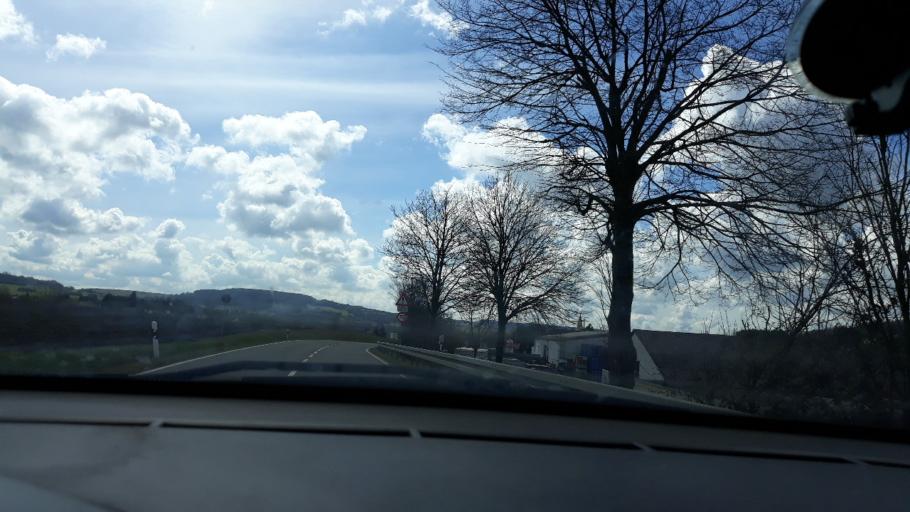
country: DE
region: Saarland
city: Gersheim
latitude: 49.1559
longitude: 7.2123
